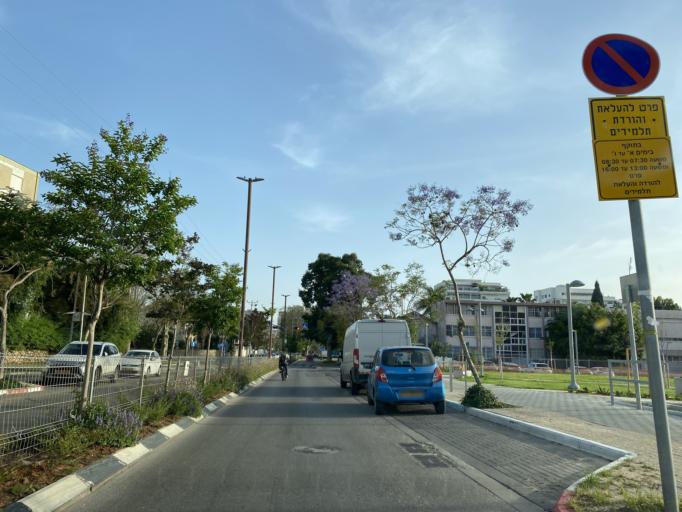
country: IL
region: Tel Aviv
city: Herzliyya
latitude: 32.1659
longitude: 34.8307
